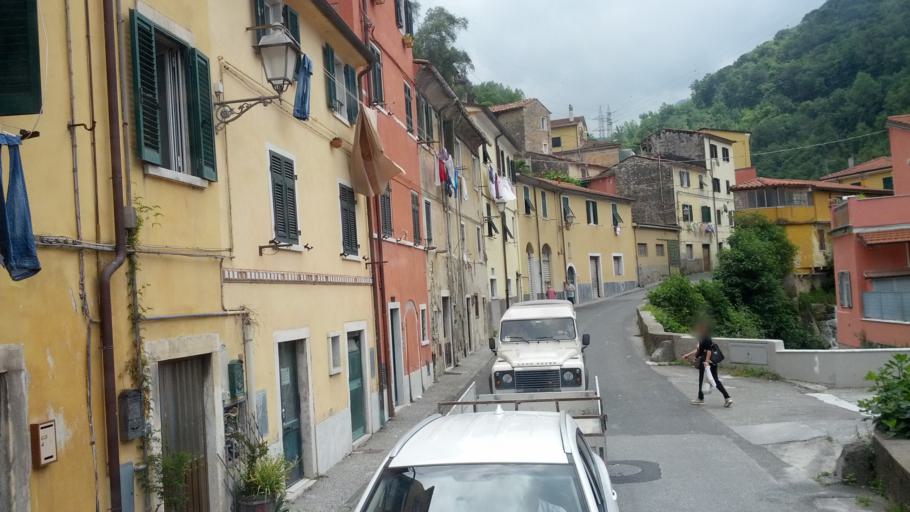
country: IT
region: Tuscany
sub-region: Provincia di Massa-Carrara
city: Carrara
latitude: 44.0825
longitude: 10.1046
